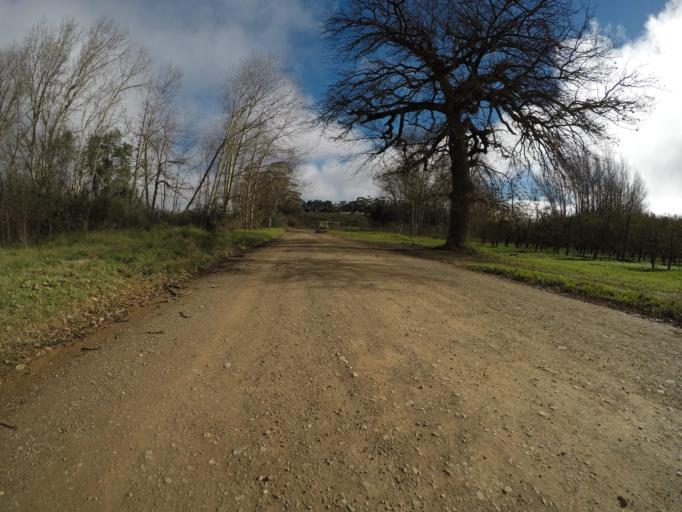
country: ZA
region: Western Cape
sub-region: Cape Winelands District Municipality
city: Ashton
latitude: -34.1256
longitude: 19.8120
